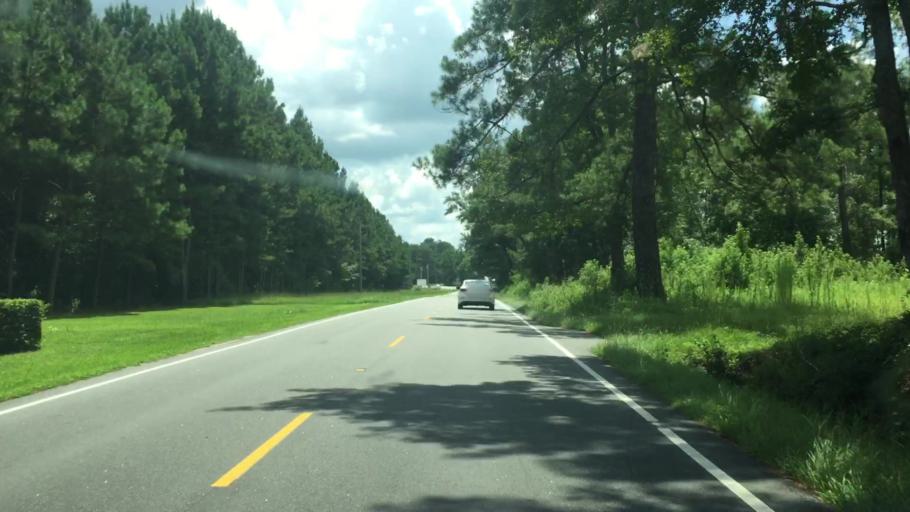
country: US
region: North Carolina
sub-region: Columbus County
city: Chadbourn
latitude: 34.2976
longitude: -78.8264
